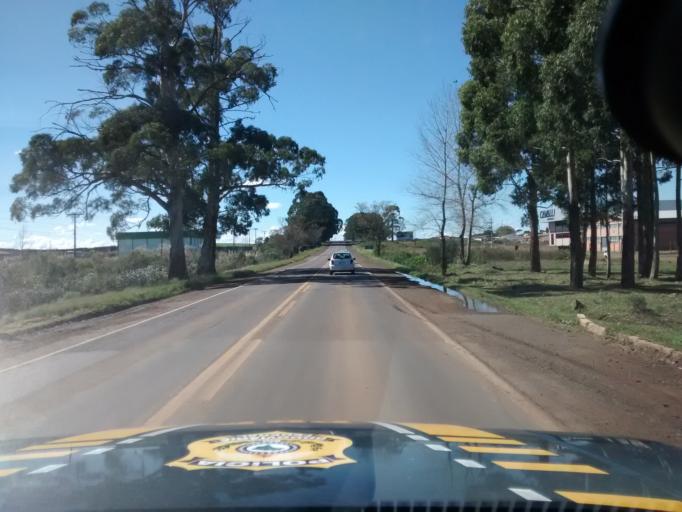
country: BR
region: Rio Grande do Sul
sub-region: Vacaria
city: Vacaria
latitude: -28.4980
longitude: -50.9170
